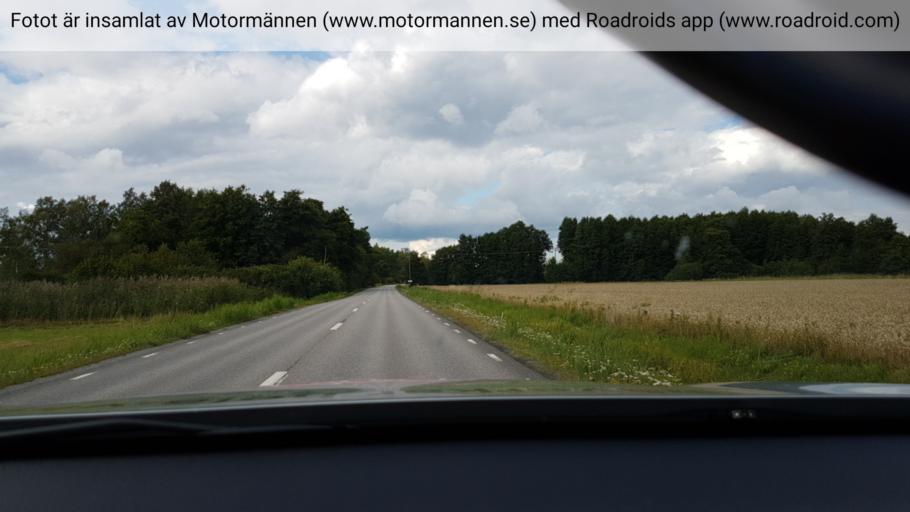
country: SE
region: Stockholm
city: Stenhamra
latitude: 59.3584
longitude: 17.7195
